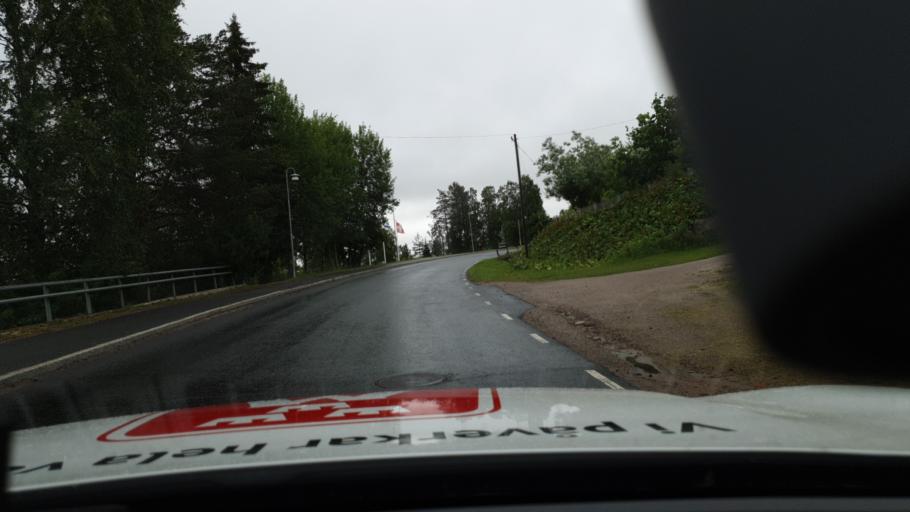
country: SE
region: Norrbotten
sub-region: Overtornea Kommun
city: OEvertornea
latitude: 66.3944
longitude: 23.6451
